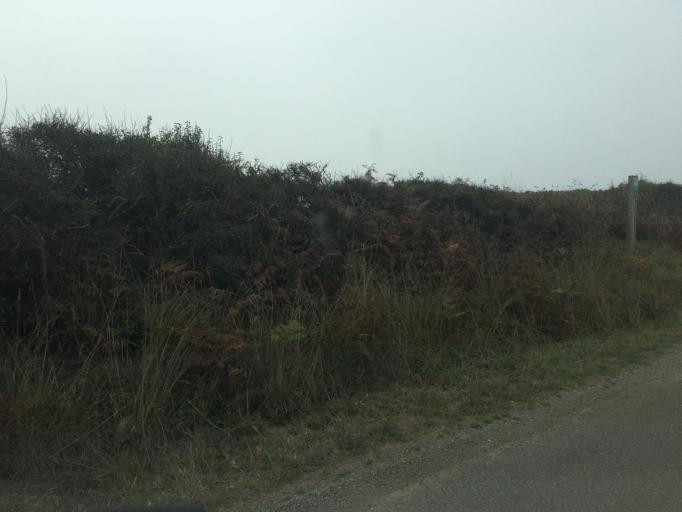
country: FR
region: Brittany
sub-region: Departement du Finistere
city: Plogoff
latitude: 48.0594
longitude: -4.7073
